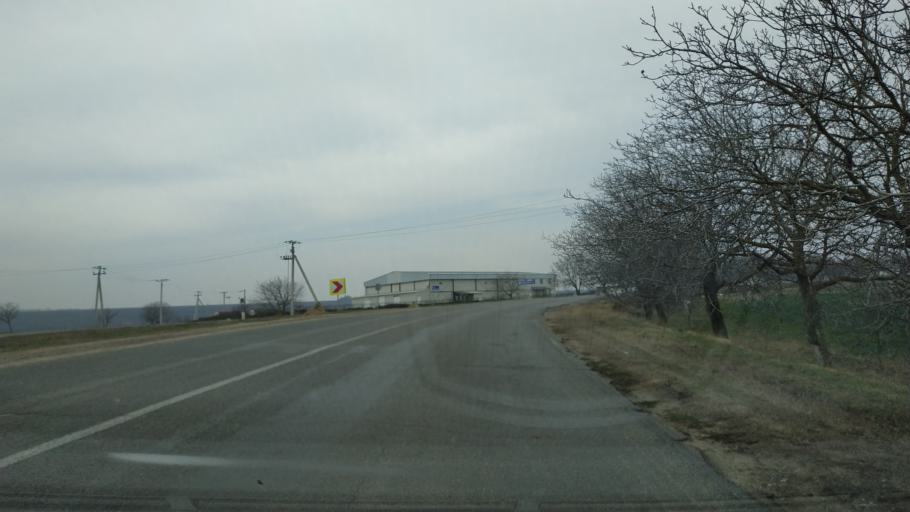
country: MD
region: Cahul
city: Cahul
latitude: 45.9326
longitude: 28.3396
